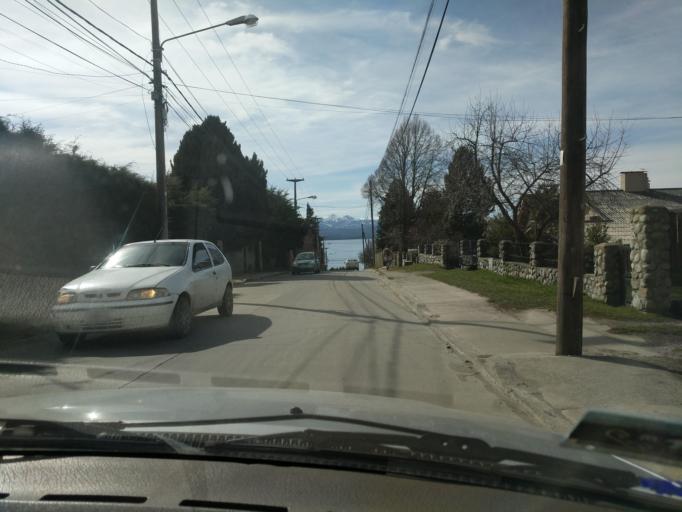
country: AR
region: Rio Negro
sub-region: Departamento de Bariloche
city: San Carlos de Bariloche
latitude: -41.1282
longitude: -71.3551
